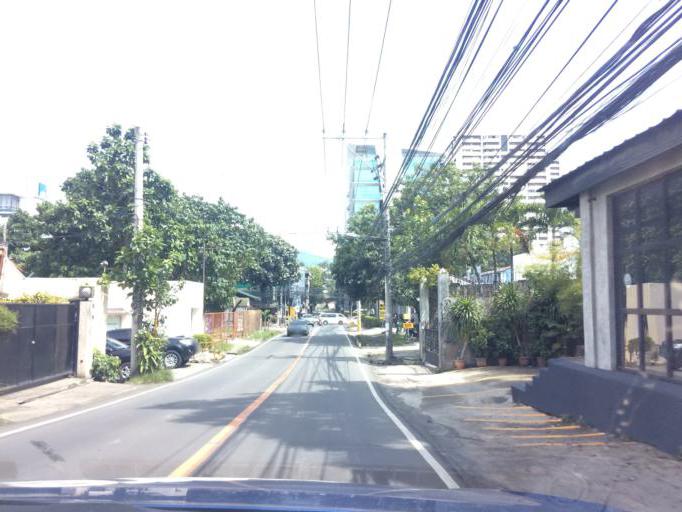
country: PH
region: Central Visayas
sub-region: Province of Cebu
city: Cebu City
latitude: 10.3160
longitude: 123.8937
